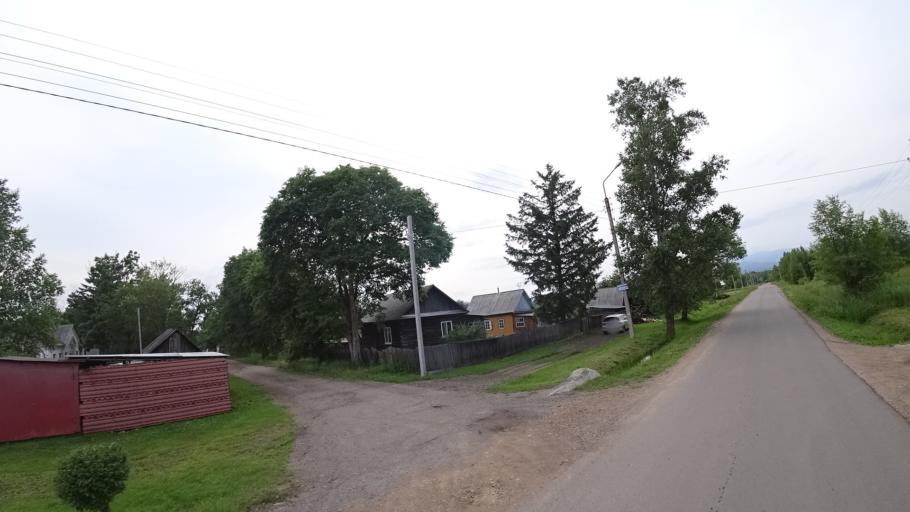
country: RU
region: Primorskiy
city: Novosysoyevka
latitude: 44.2337
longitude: 133.3596
